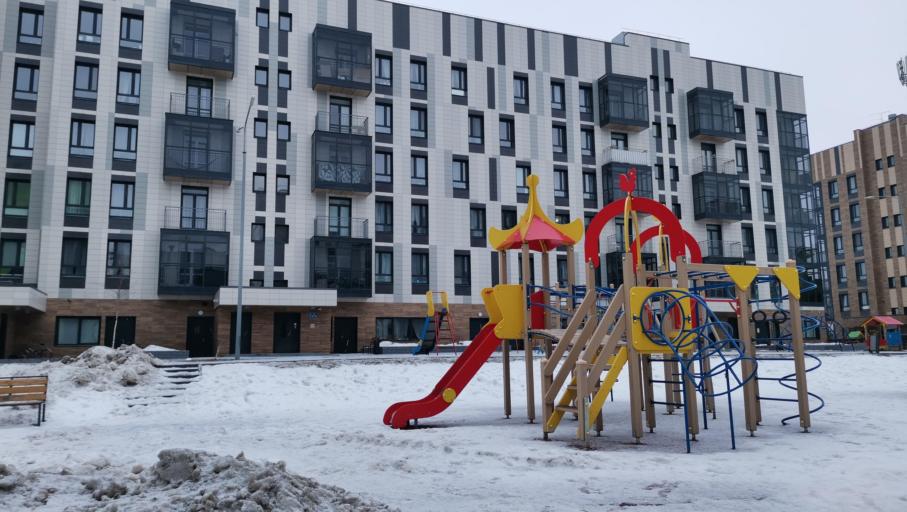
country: RU
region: Tatarstan
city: Sviyazhsk
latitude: 55.7489
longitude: 48.7450
